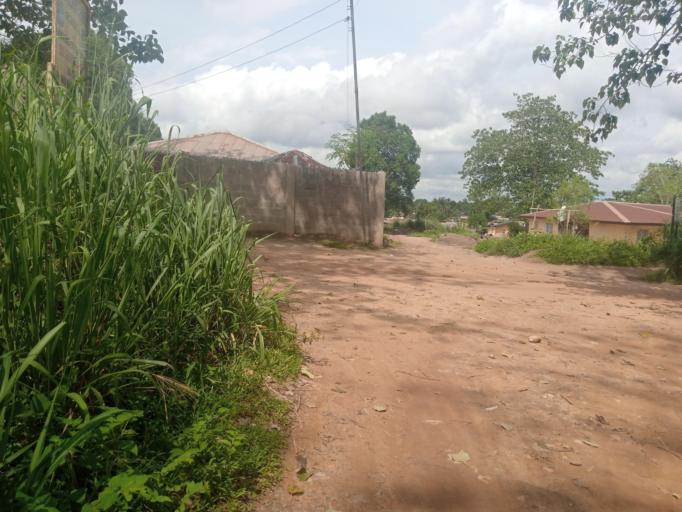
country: SL
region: Southern Province
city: Bo
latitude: 7.9658
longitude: -11.7562
